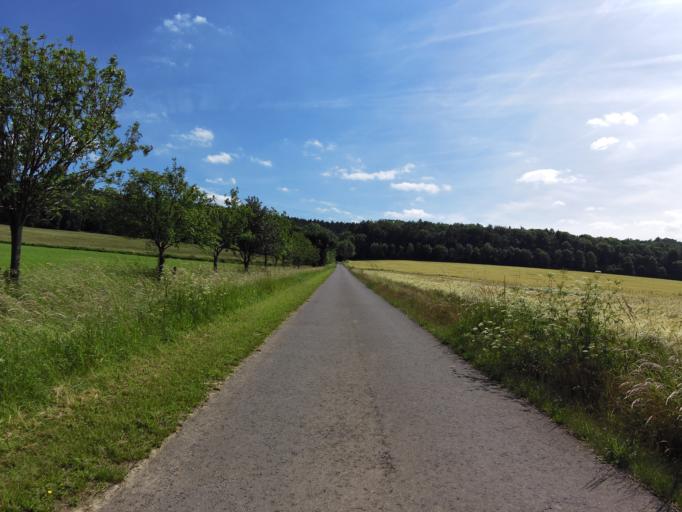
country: DE
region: Thuringia
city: Seebach
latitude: 50.9722
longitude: 10.4329
